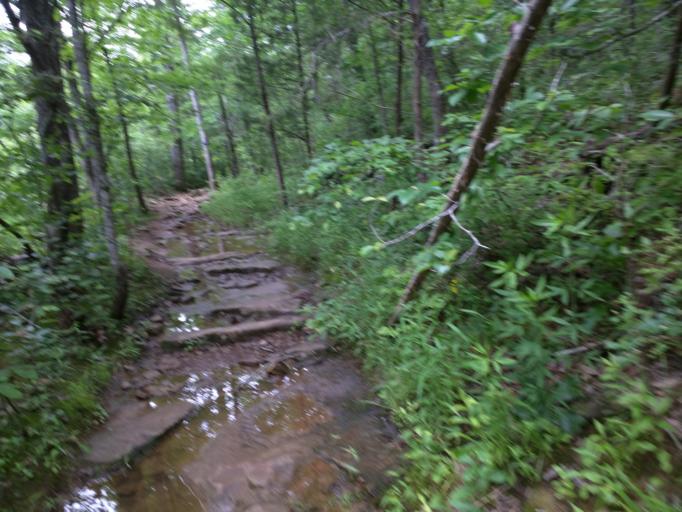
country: US
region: Arkansas
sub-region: Madison County
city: Huntsville
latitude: 35.8987
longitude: -93.5761
